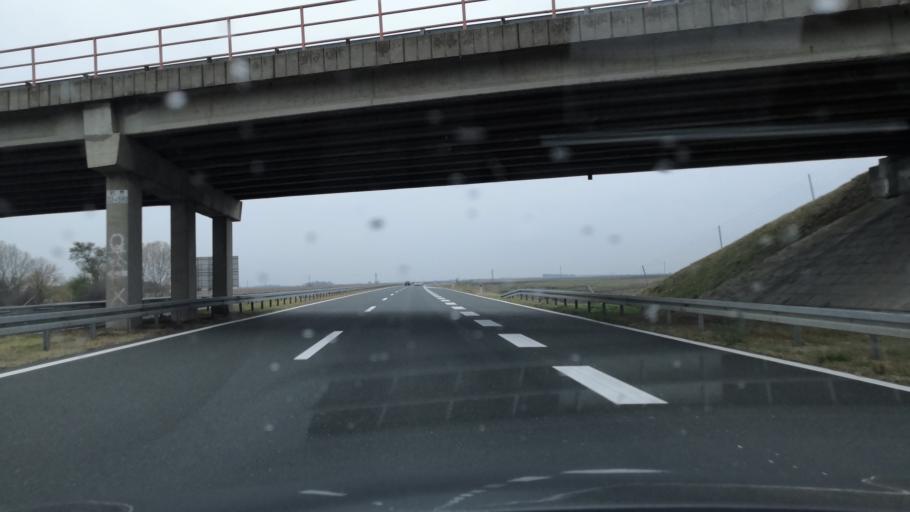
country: RS
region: Autonomna Pokrajina Vojvodina
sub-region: Severnobacki Okrug
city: Subotica
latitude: 45.9703
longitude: 19.7109
